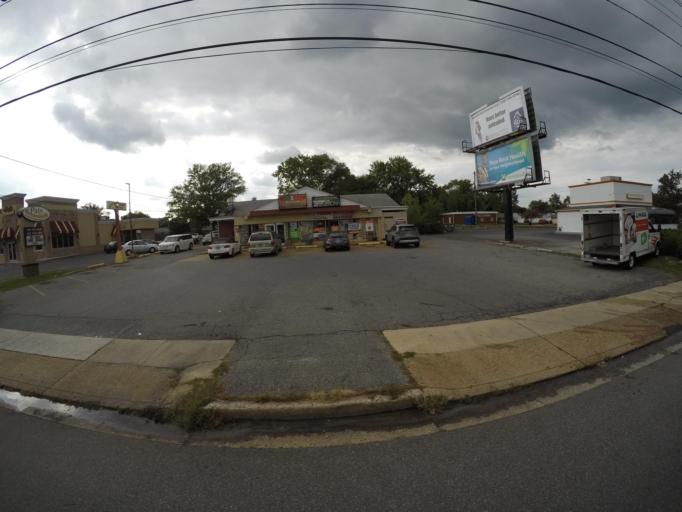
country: US
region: Delaware
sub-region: New Castle County
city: Brookside
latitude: 39.6648
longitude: -75.7269
